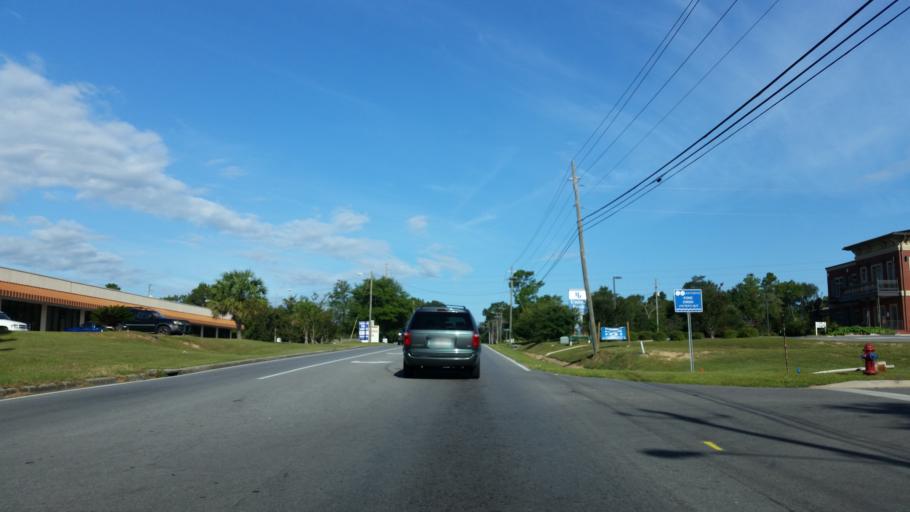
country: US
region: Florida
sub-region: Santa Rosa County
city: Milton
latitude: 30.6335
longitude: -87.0700
